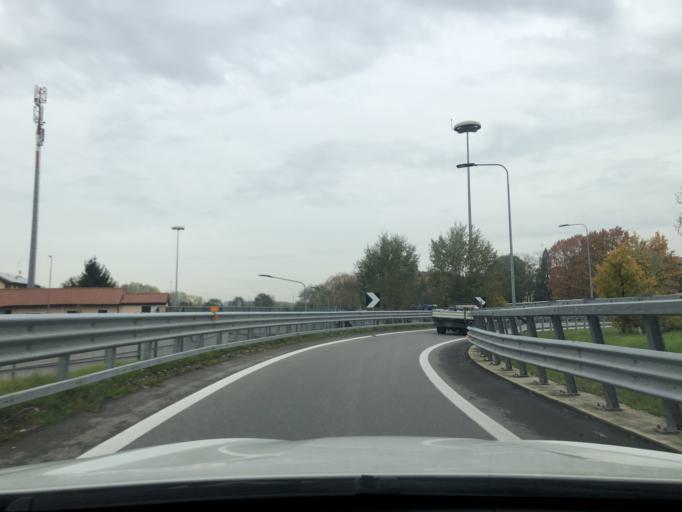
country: IT
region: Lombardy
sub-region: Citta metropolitana di Milano
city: Novegro-Tregarezzo-San Felice
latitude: 45.4881
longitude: 9.2533
